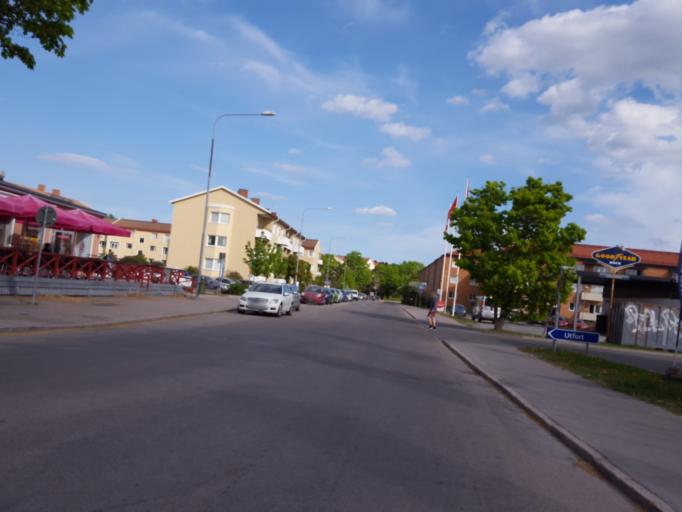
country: SE
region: Uppsala
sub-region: Uppsala Kommun
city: Uppsala
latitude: 59.8680
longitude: 17.6617
